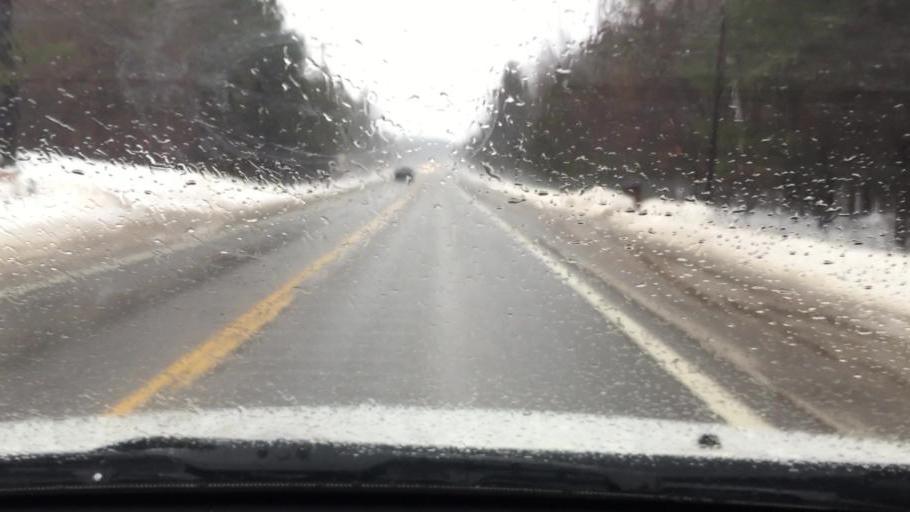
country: US
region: Michigan
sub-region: Charlevoix County
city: East Jordan
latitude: 45.2295
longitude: -85.1817
